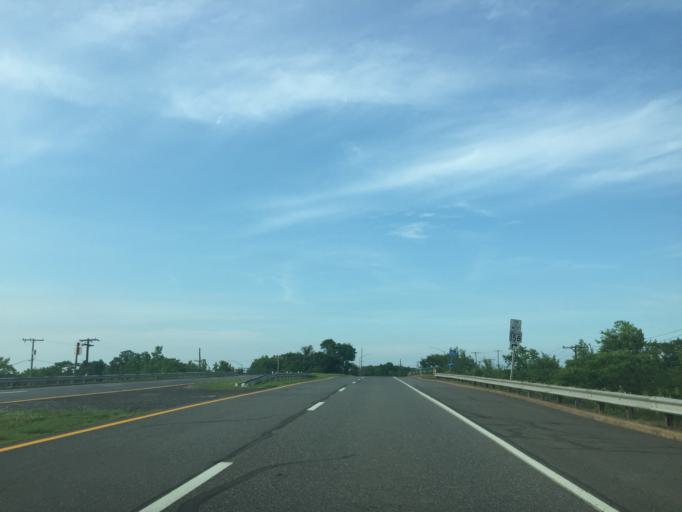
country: US
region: Maryland
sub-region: Baltimore County
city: Edgemere
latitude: 39.2300
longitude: -76.4658
